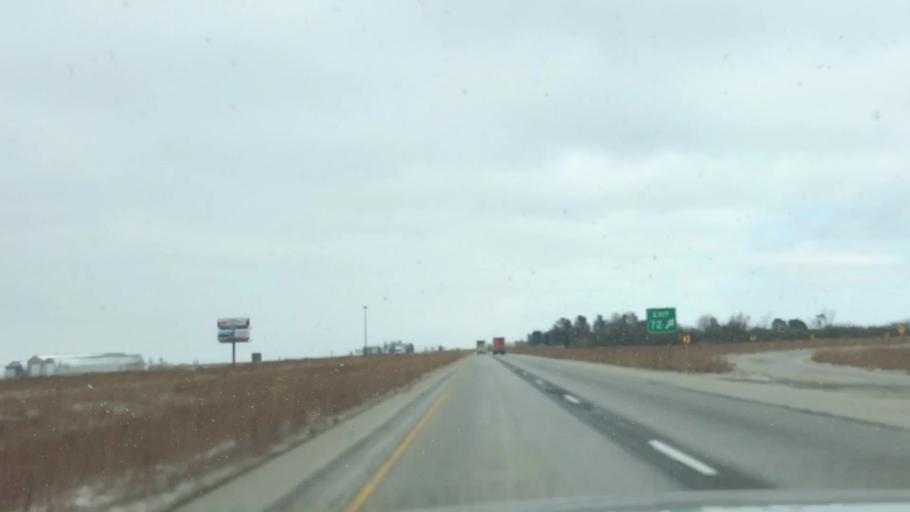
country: US
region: Illinois
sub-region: Sangamon County
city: Divernon
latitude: 39.4459
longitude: -89.6439
